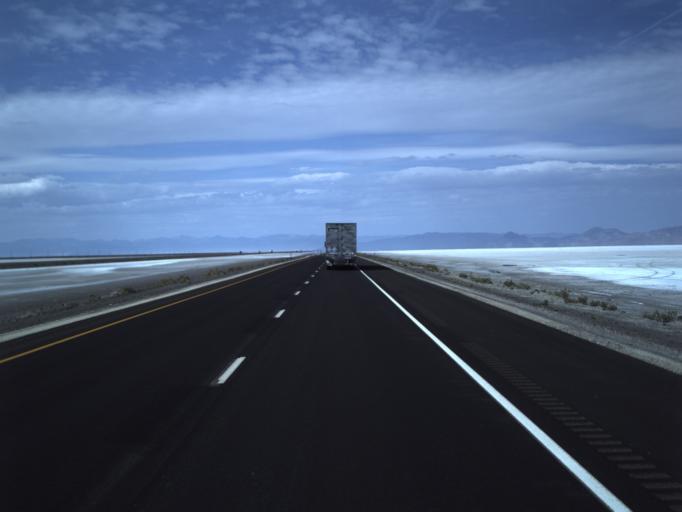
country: US
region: Utah
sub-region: Tooele County
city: Wendover
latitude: 40.7344
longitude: -113.6120
